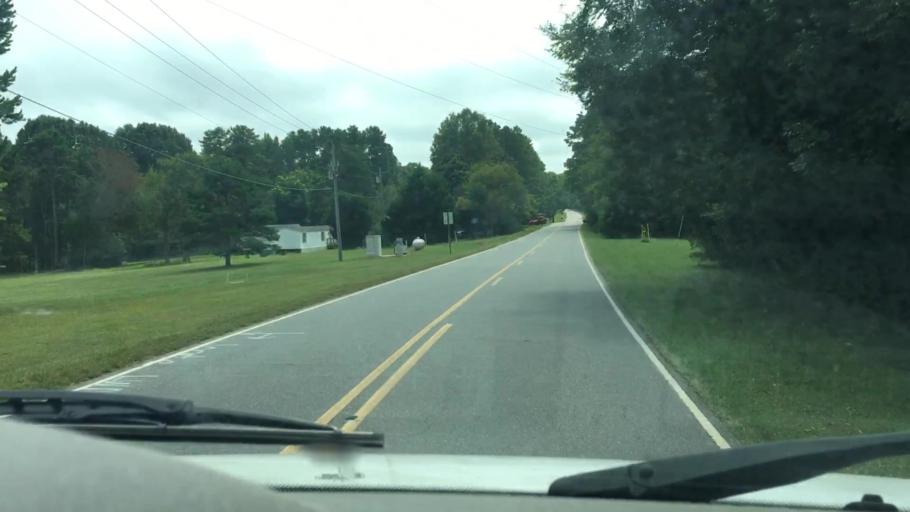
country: US
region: North Carolina
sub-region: Gaston County
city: Davidson
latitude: 35.5147
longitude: -80.7988
